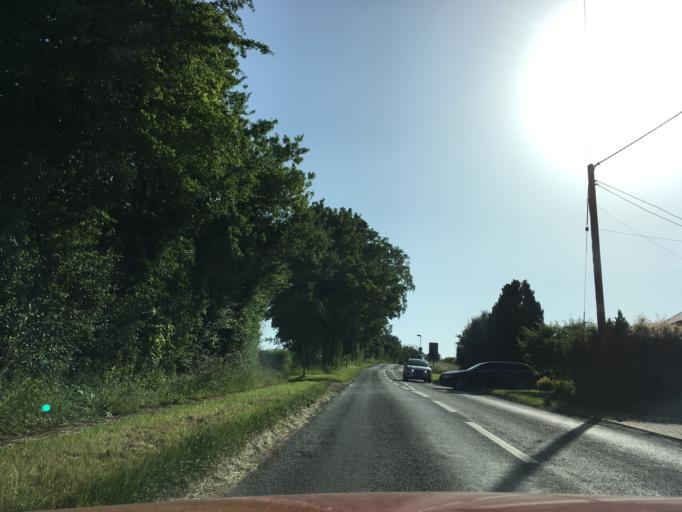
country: GB
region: England
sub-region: Oxfordshire
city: Deddington
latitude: 51.9271
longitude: -1.3788
